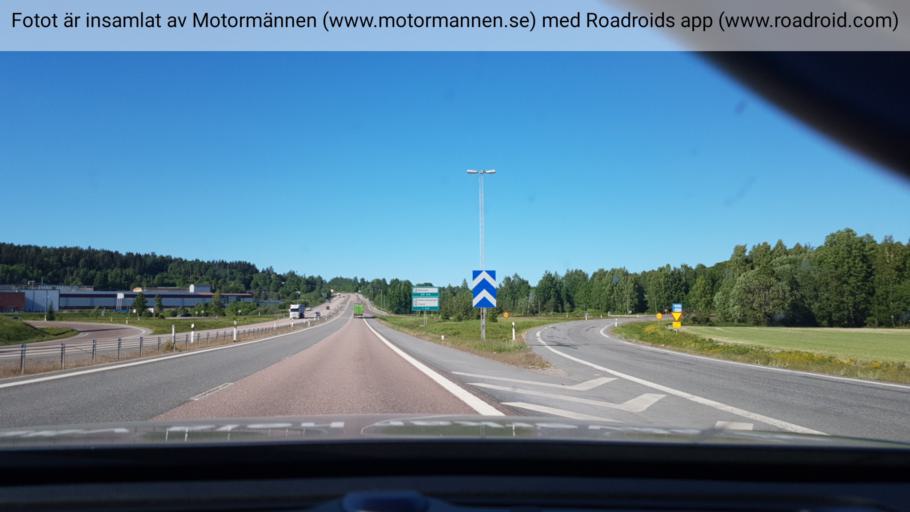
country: SE
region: Vaesternorrland
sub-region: Sundsvalls Kommun
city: Sundsbruk
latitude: 62.4456
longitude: 17.3389
